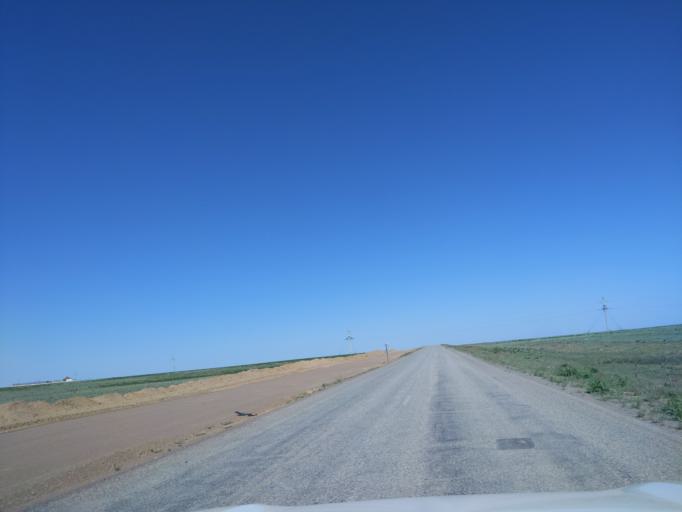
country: KZ
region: Almaty Oblysy
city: Bakanas
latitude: 44.1839
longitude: 75.7952
